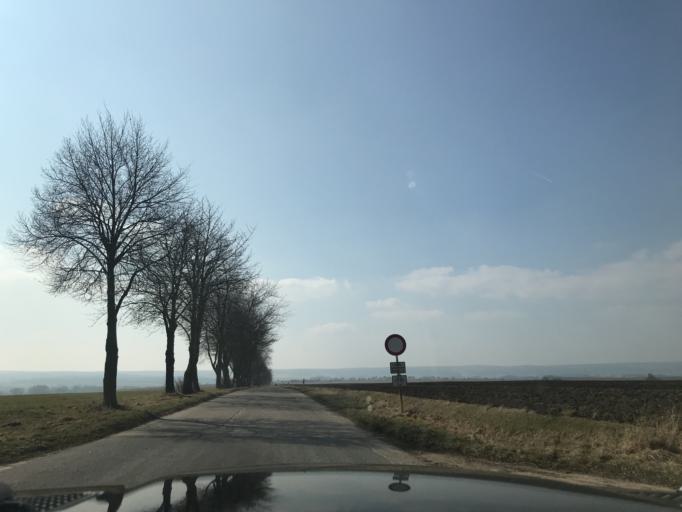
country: DE
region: Thuringia
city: Heroldishausen
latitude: 51.1410
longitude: 10.5076
